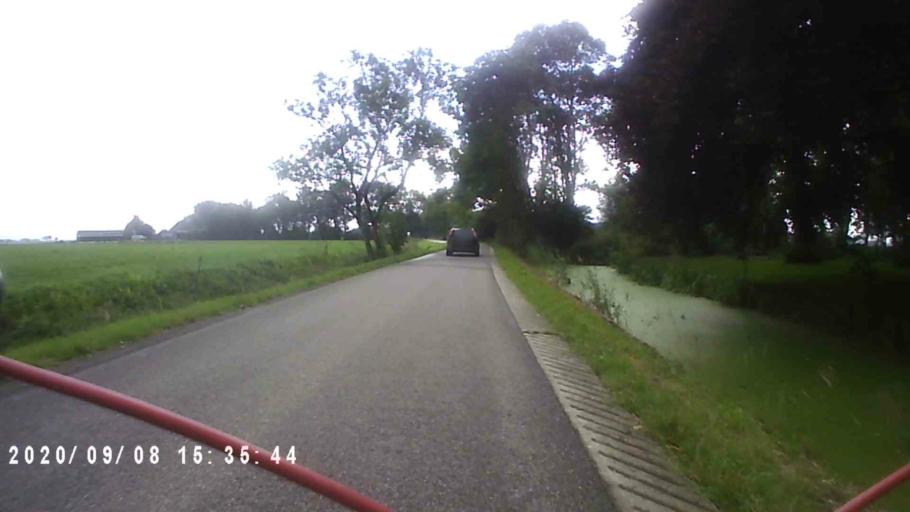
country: NL
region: Groningen
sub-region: Gemeente Bedum
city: Bedum
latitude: 53.2844
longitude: 6.6283
